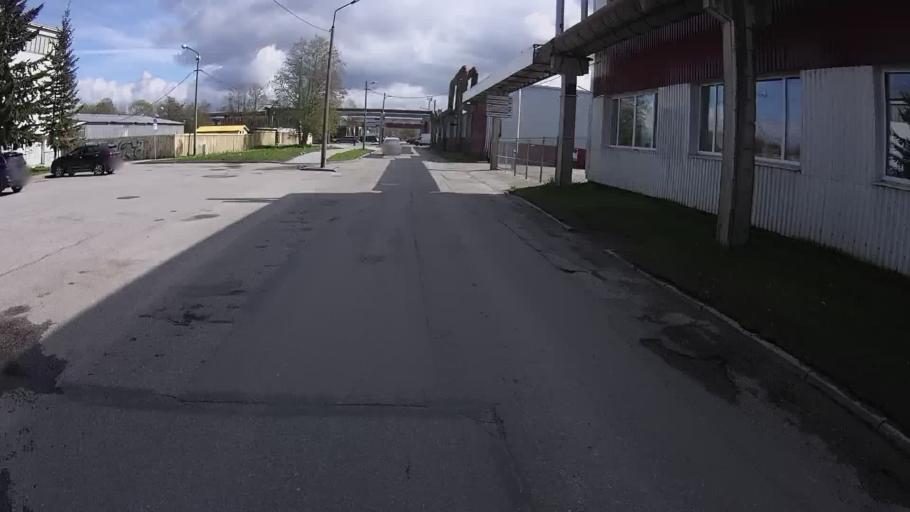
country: EE
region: Harju
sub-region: Tallinna linn
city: Tallinn
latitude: 59.4202
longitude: 24.6862
